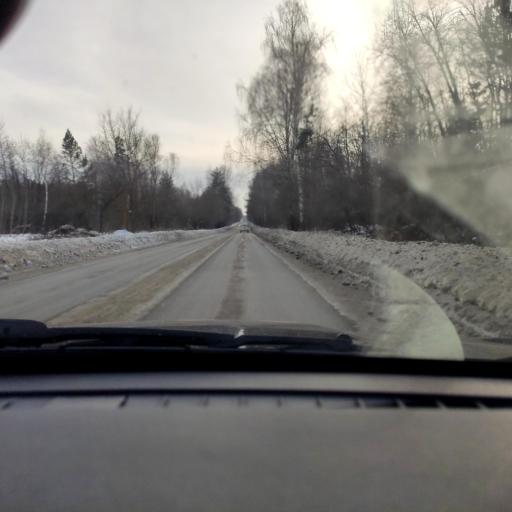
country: RU
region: Samara
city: Pribrezhnyy
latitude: 53.5100
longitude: 49.8504
